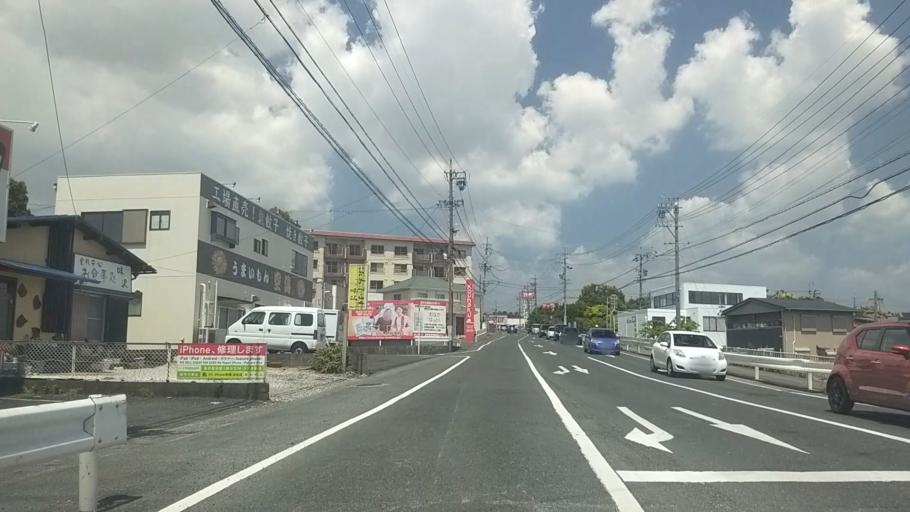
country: JP
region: Shizuoka
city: Hamamatsu
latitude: 34.7507
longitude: 137.7363
